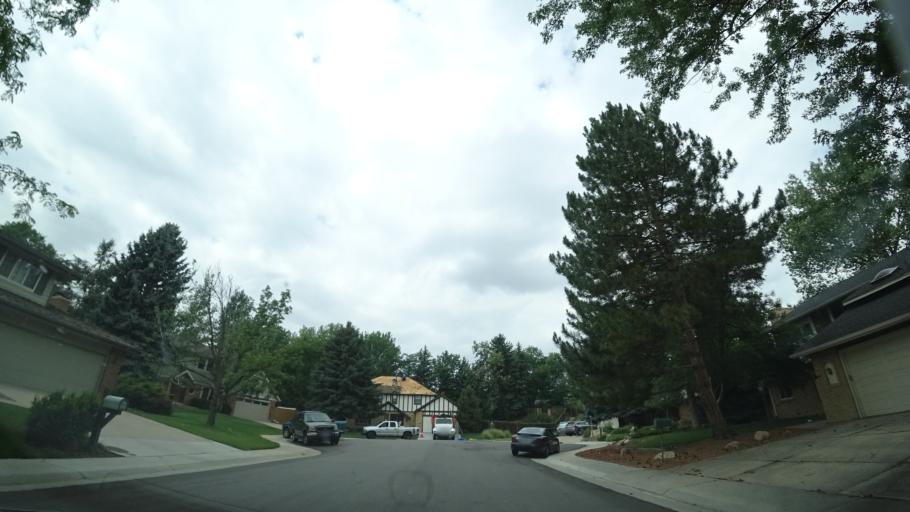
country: US
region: Colorado
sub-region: Jefferson County
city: West Pleasant View
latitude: 39.7219
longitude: -105.1587
